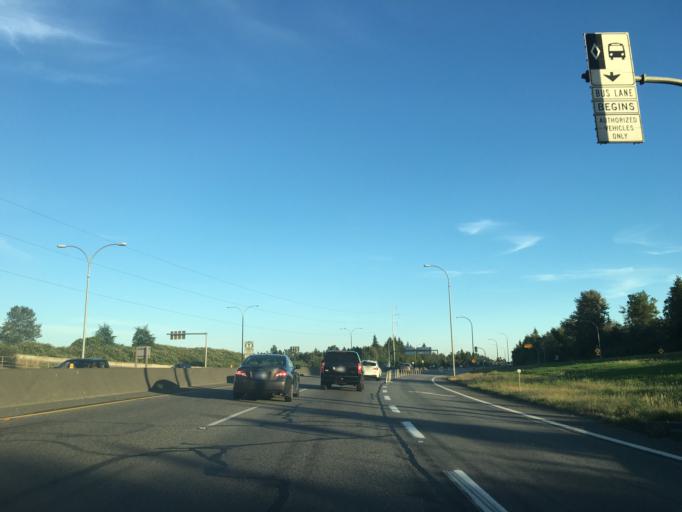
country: CA
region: British Columbia
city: Richmond
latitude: 49.1703
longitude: -123.0870
